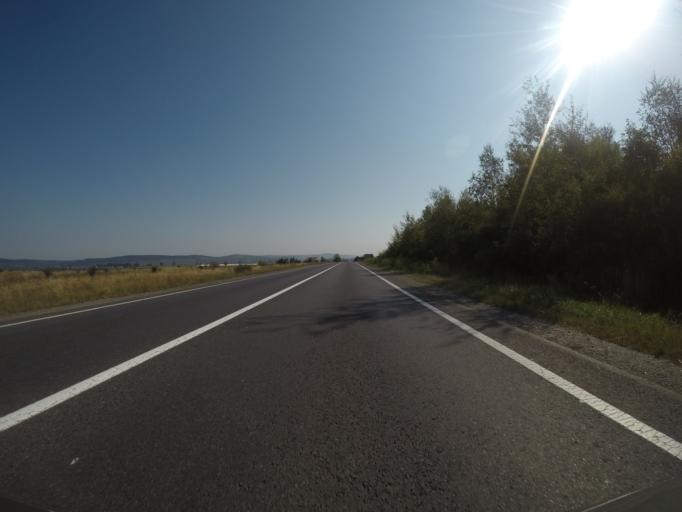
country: RO
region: Sibiu
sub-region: Comuna Carta
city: Carta
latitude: 45.7612
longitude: 24.5663
